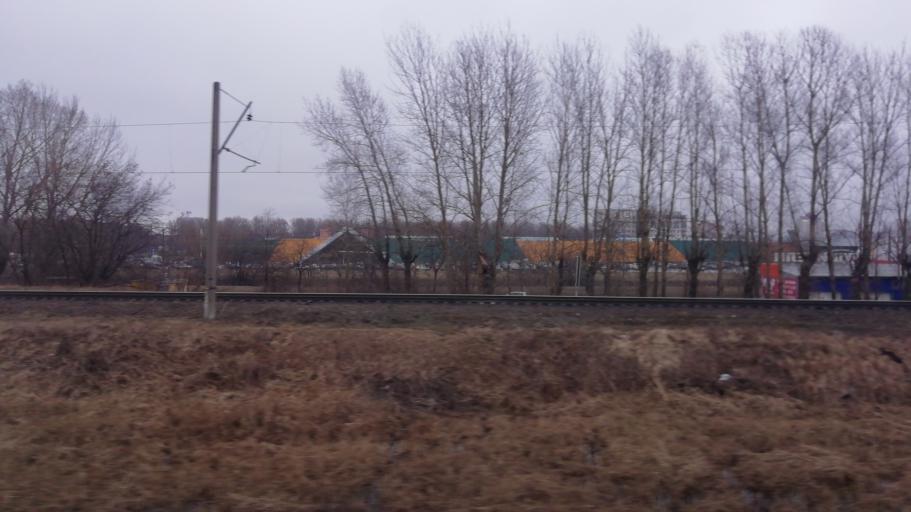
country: RU
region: St.-Petersburg
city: Kupchino
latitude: 59.8766
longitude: 30.3522
